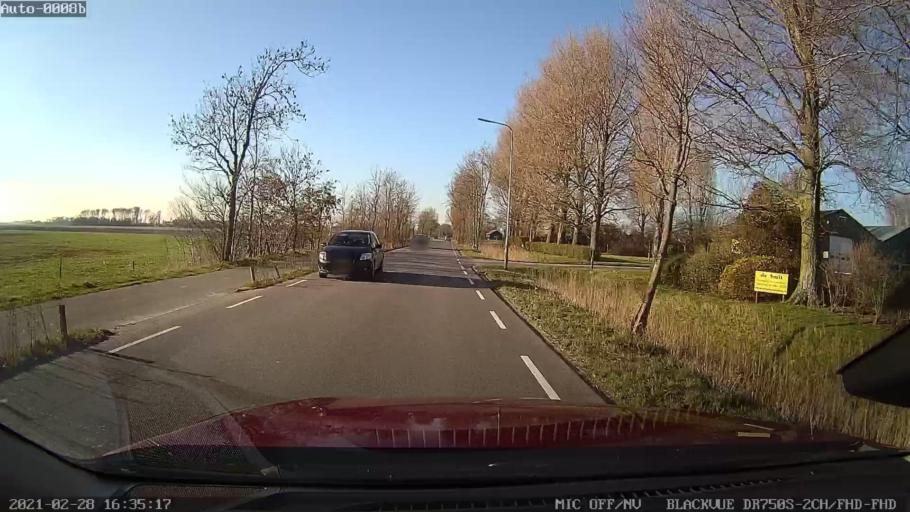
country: NL
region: Zeeland
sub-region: Gemeente Middelburg
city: Middelburg
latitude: 51.5100
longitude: 3.5815
